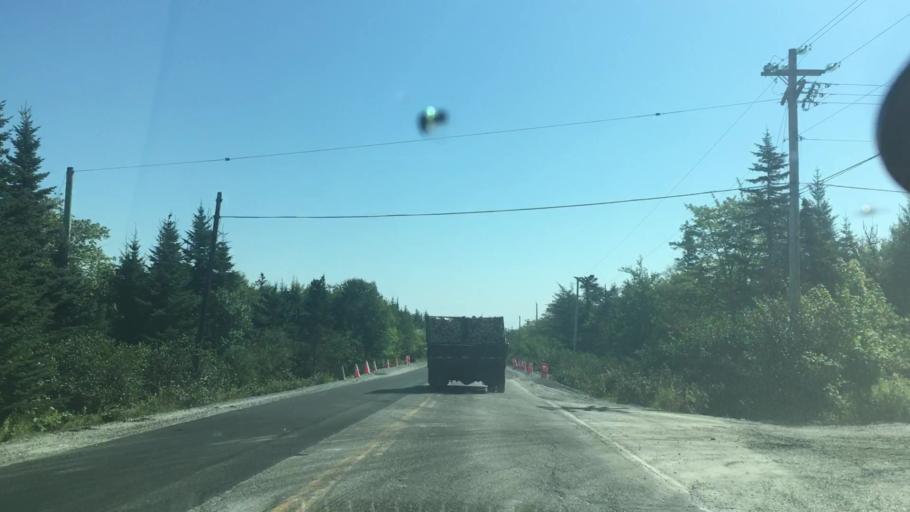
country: CA
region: Nova Scotia
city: New Glasgow
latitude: 44.8991
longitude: -62.4361
